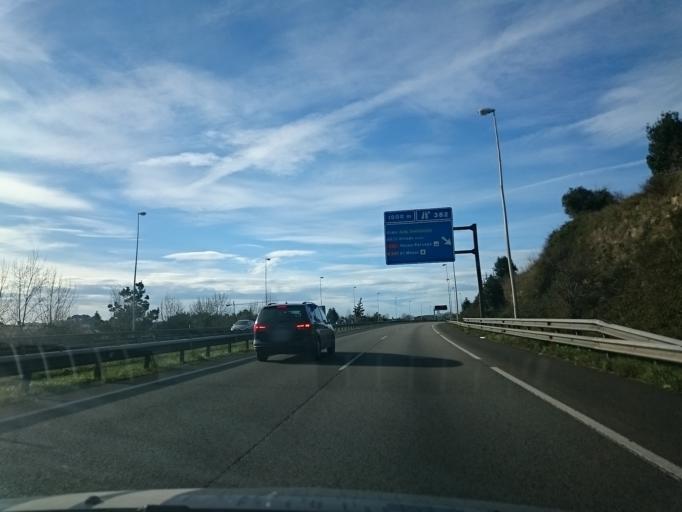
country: ES
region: Asturias
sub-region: Province of Asturias
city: Gijon
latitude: 43.5134
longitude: -5.6687
